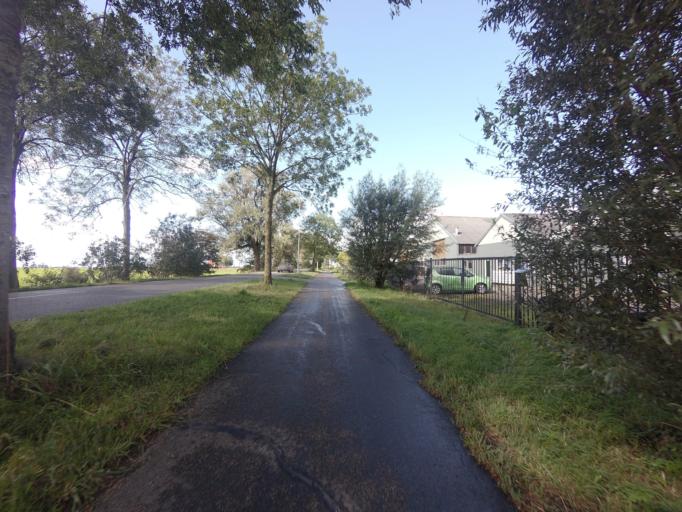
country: NL
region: Friesland
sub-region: Gemeente Boarnsterhim
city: Warten
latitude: 53.1497
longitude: 5.8817
